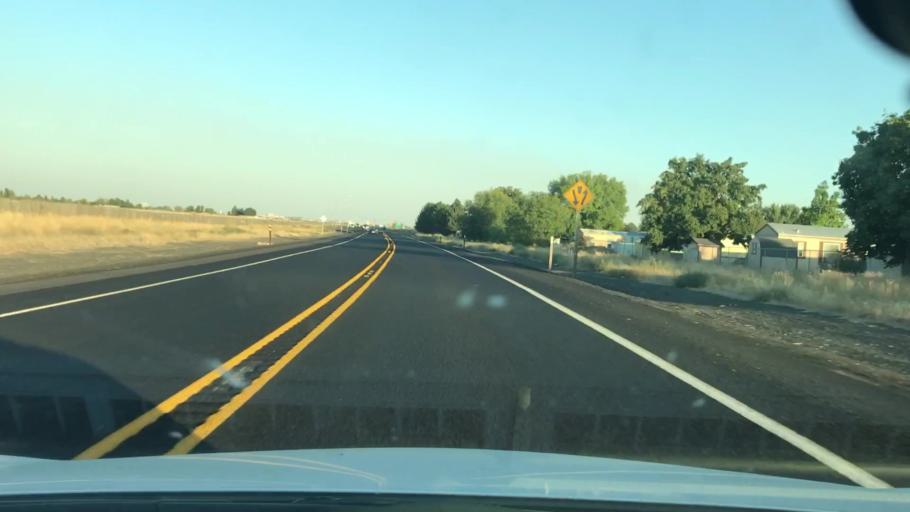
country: US
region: Washington
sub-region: Grant County
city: Cascade Valley
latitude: 47.1602
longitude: -119.3210
